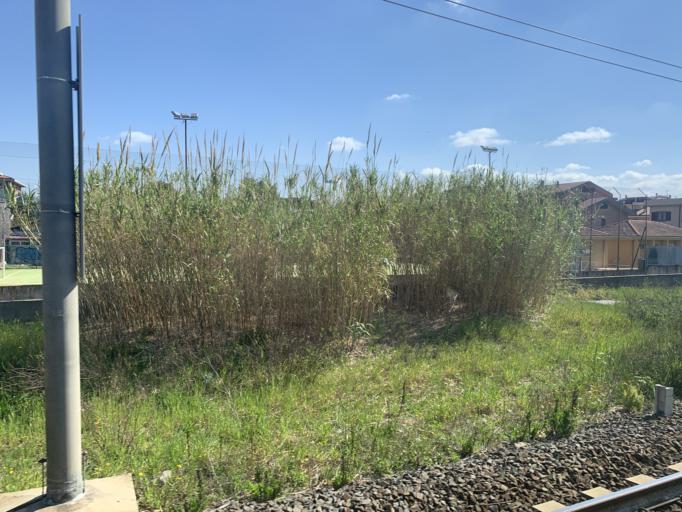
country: IT
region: Latium
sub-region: Citta metropolitana di Roma Capitale
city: Ciampino
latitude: 41.8074
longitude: 12.5930
